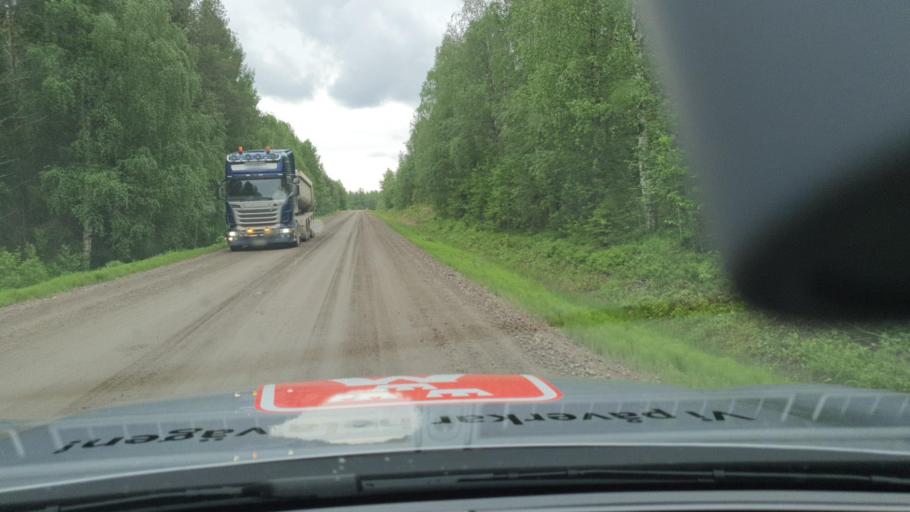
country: SE
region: Norrbotten
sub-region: Overtornea Kommun
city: OEvertornea
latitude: 66.4152
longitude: 23.5917
